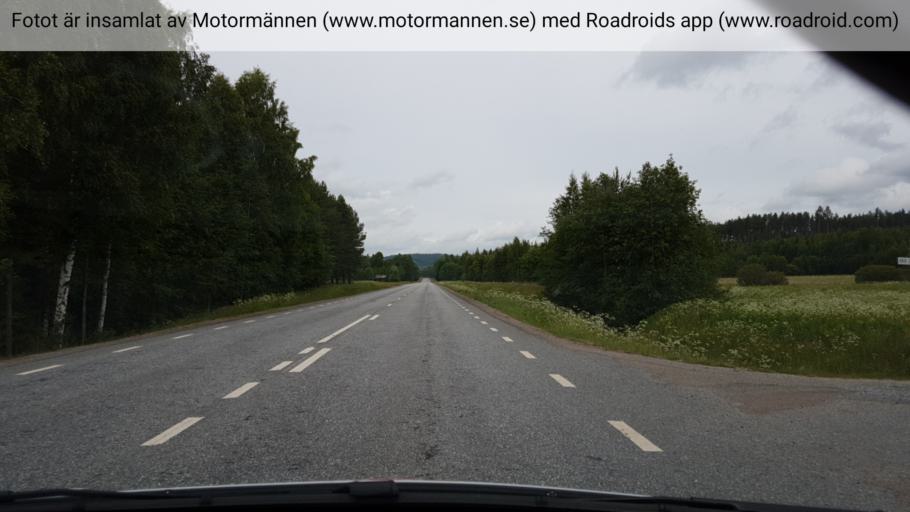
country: SE
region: Vaesternorrland
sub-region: Solleftea Kommun
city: Solleftea
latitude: 63.2609
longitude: 17.2168
